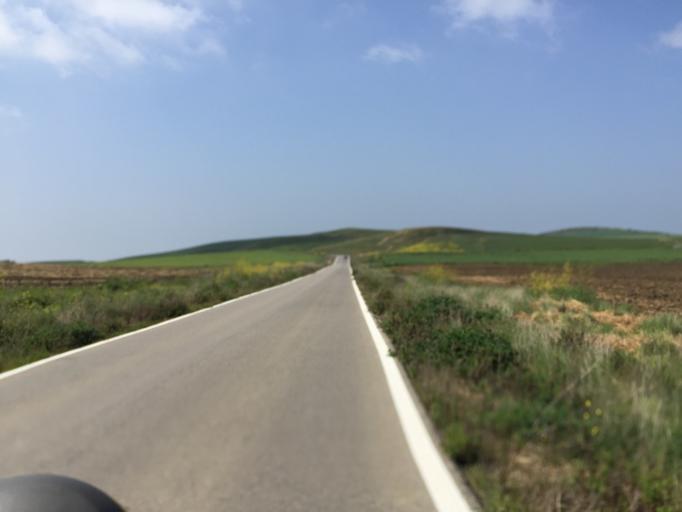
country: ES
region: Andalusia
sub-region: Provincia de Cadiz
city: Vejer de la Frontera
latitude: 36.2358
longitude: -6.0238
